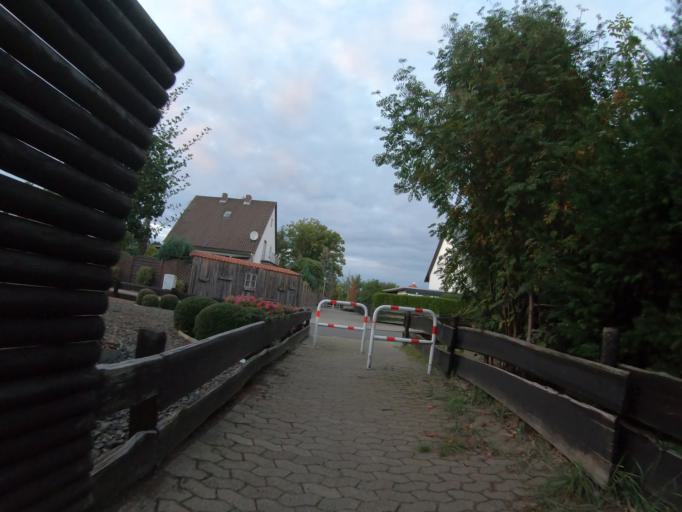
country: DE
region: Lower Saxony
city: Gifhorn
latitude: 52.4736
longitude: 10.5662
